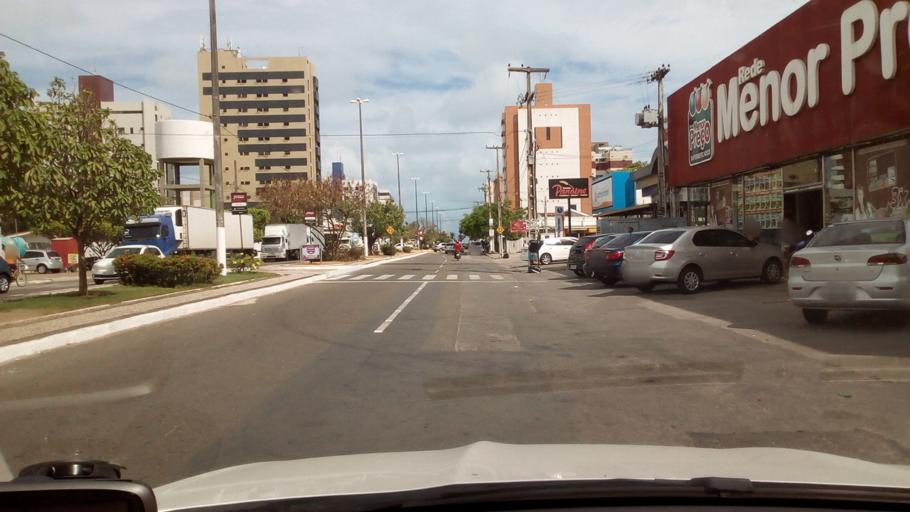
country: BR
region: Paraiba
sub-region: Cabedelo
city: Cabedelo
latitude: -7.0436
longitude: -34.8458
